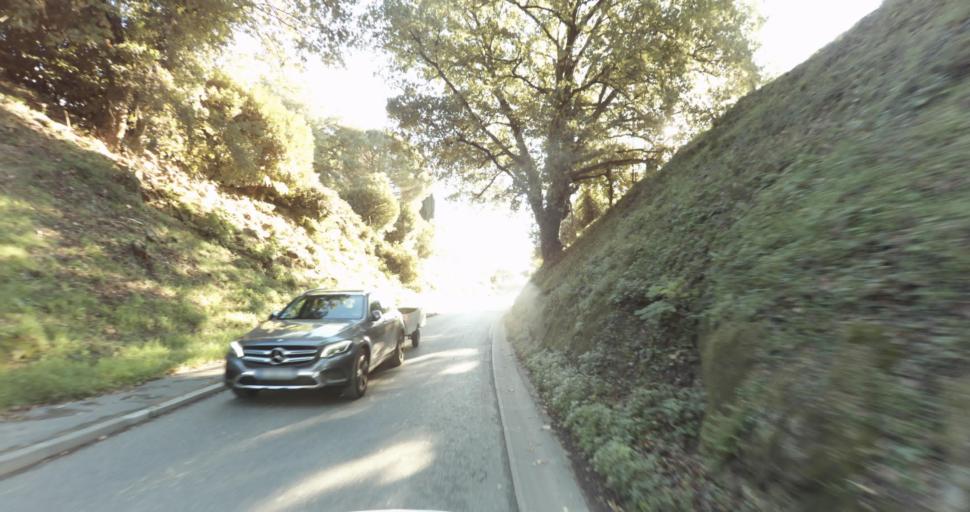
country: FR
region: Provence-Alpes-Cote d'Azur
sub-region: Departement des Alpes-Maritimes
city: Tourrettes-sur-Loup
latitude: 43.7214
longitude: 7.0810
